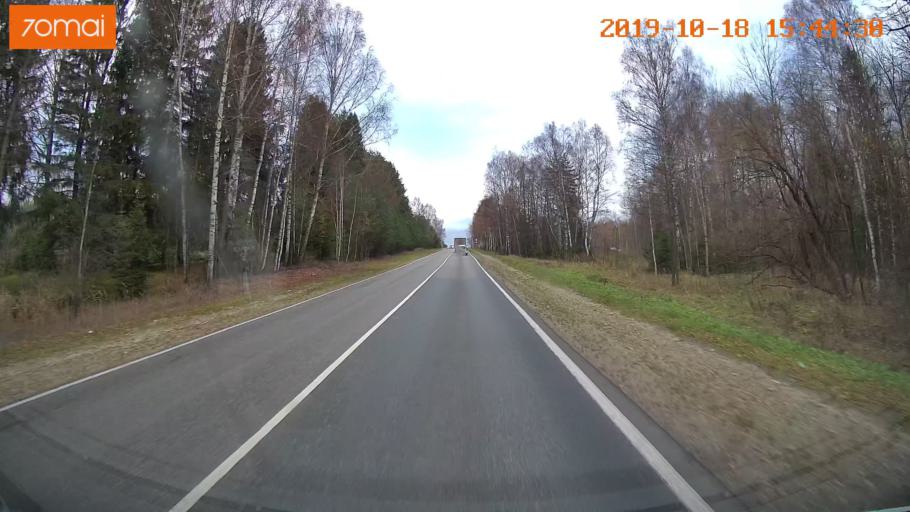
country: RU
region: Vladimir
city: Golovino
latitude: 55.9823
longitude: 40.5510
